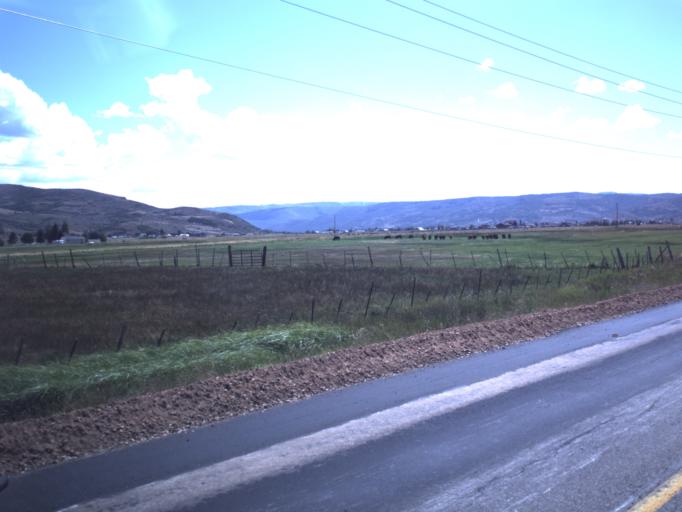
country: US
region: Utah
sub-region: Summit County
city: Kamas
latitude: 40.6281
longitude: -111.2807
